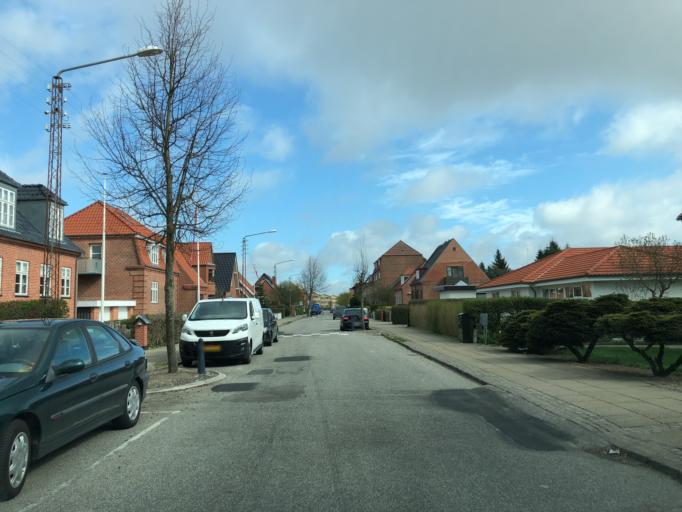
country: DK
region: North Denmark
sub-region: Alborg Kommune
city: Aalborg
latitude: 57.0518
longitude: 9.8962
